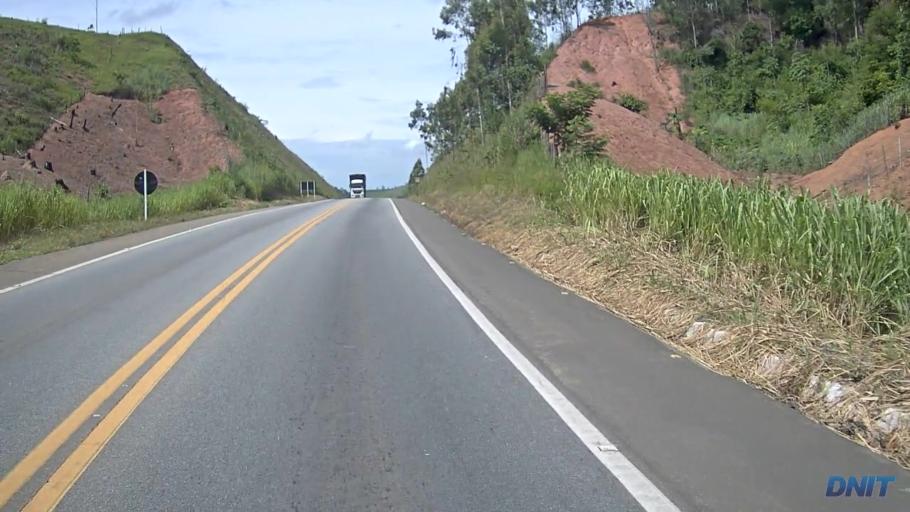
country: BR
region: Minas Gerais
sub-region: Ipatinga
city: Ipatinga
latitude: -19.4352
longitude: -42.5091
